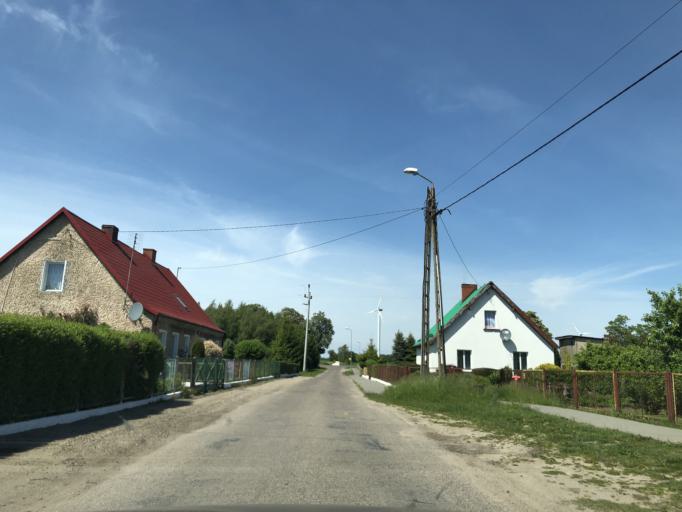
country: PL
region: West Pomeranian Voivodeship
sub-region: Powiat kolobrzeski
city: Goscino
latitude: 54.0505
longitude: 15.7284
